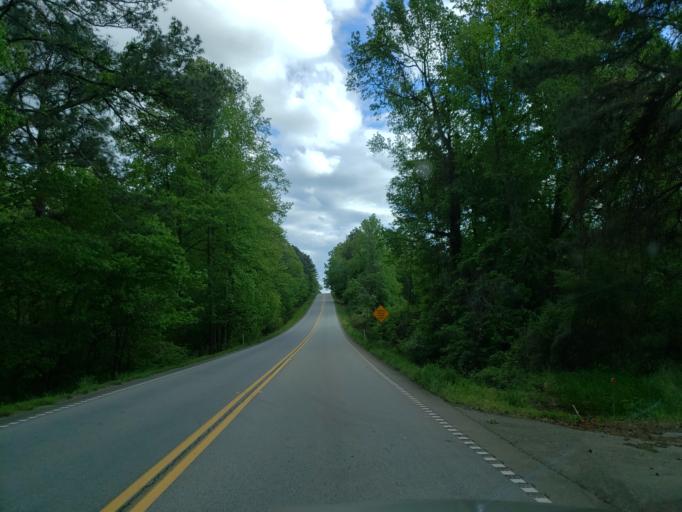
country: US
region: Georgia
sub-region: Haralson County
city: Tallapoosa
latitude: 33.8548
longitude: -85.2910
